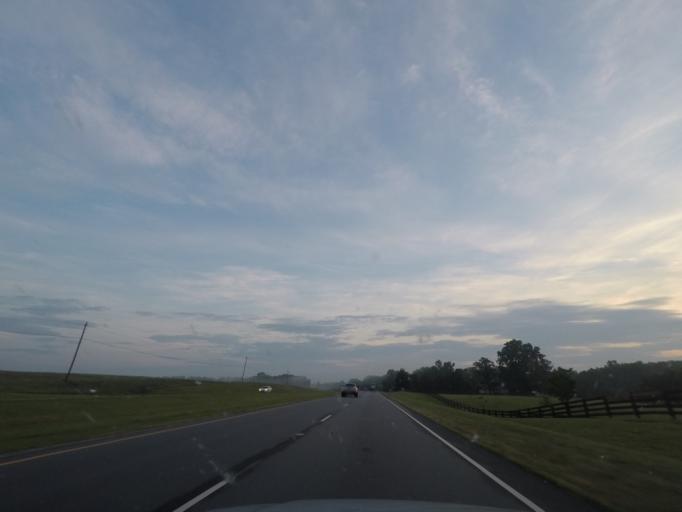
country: US
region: North Carolina
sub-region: Person County
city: Roxboro
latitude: 36.2355
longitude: -78.9321
